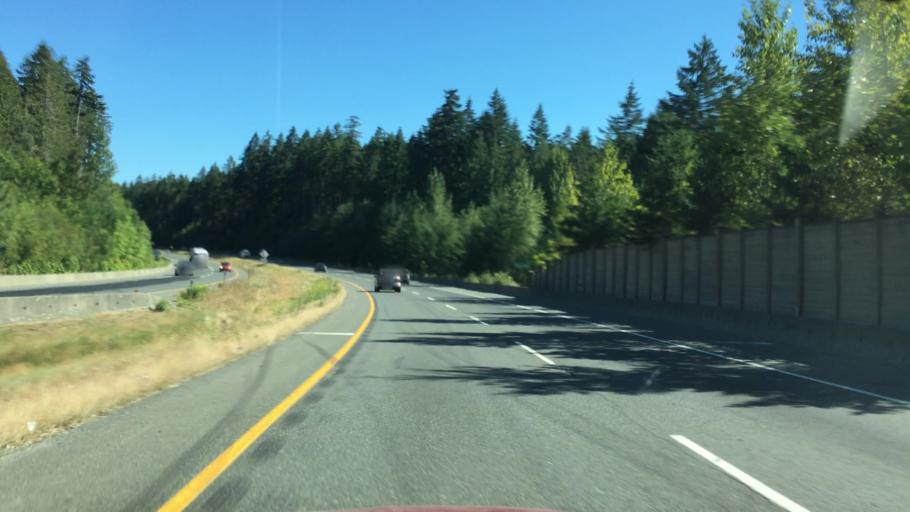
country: CA
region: British Columbia
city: Nanaimo
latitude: 49.1462
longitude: -123.9723
